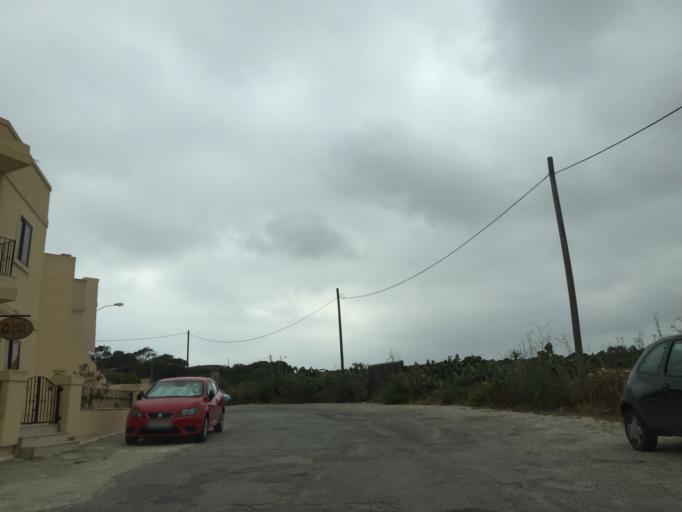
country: MT
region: L-Imgarr
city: Imgarr
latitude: 35.9231
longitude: 14.3682
